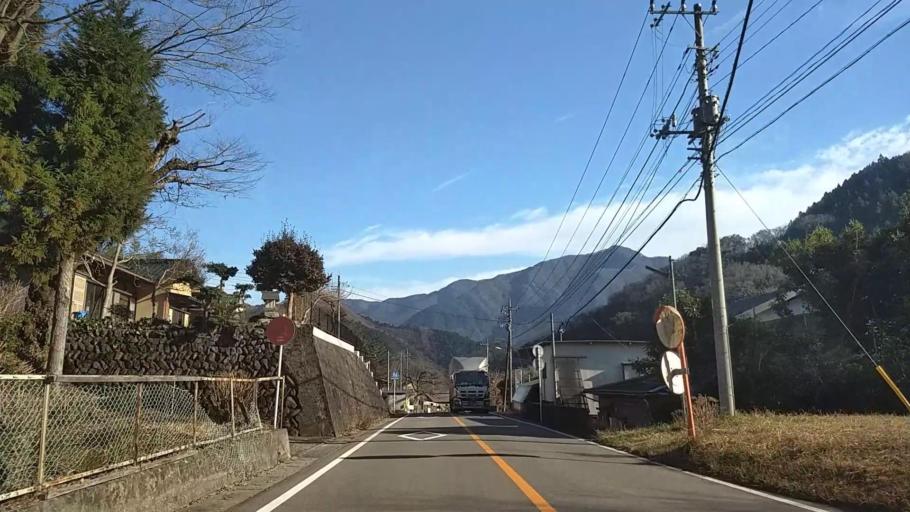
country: JP
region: Yamanashi
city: Uenohara
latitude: 35.5364
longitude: 139.0821
